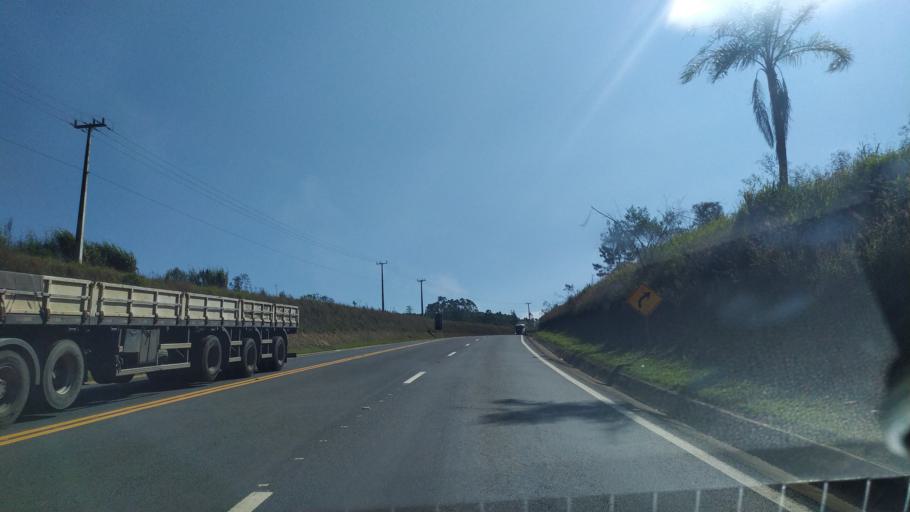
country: BR
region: Parana
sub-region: Telemaco Borba
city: Telemaco Borba
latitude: -24.2597
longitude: -50.7262
